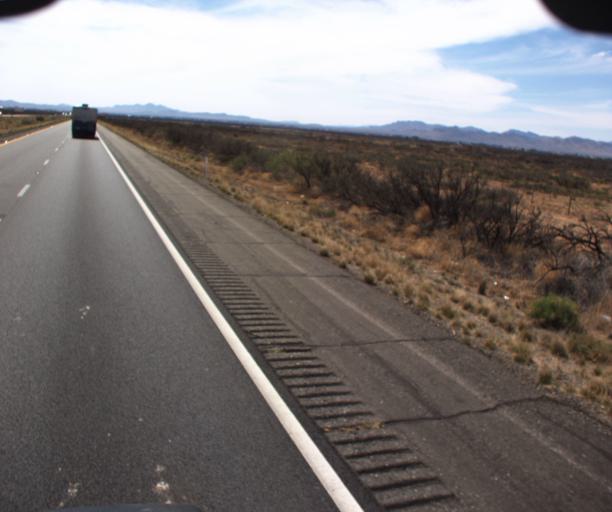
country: US
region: Arizona
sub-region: Cochise County
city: Willcox
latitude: 32.3014
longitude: -109.8047
